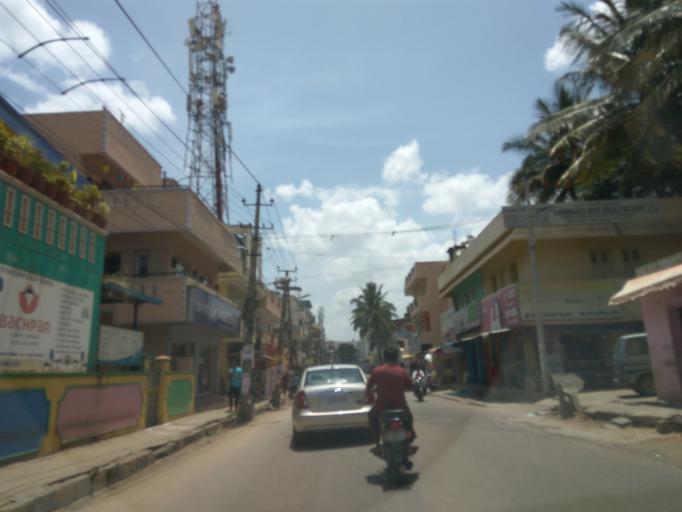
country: IN
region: Karnataka
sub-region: Bangalore Urban
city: Bangalore
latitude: 12.9850
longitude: 77.6745
